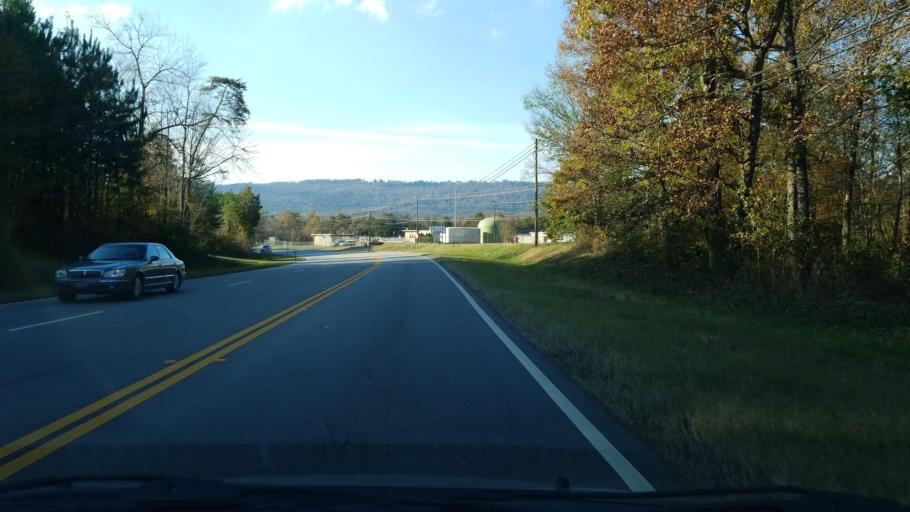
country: US
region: Georgia
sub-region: Dade County
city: Trenton
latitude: 34.8619
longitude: -85.4964
